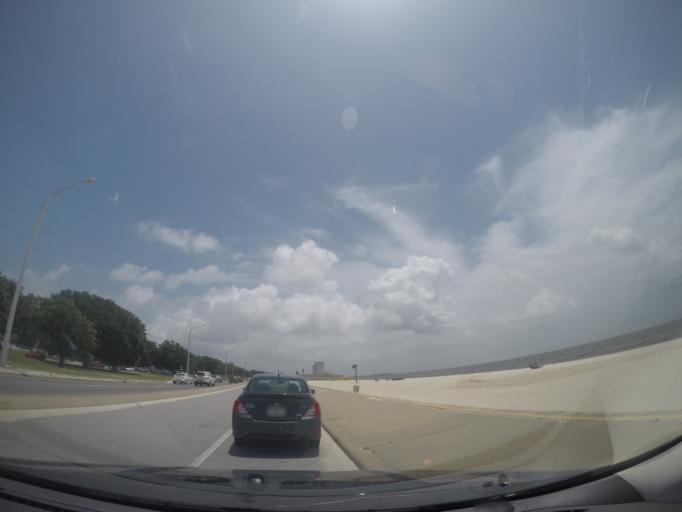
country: US
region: Mississippi
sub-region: Harrison County
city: Biloxi
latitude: 30.3943
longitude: -88.9108
